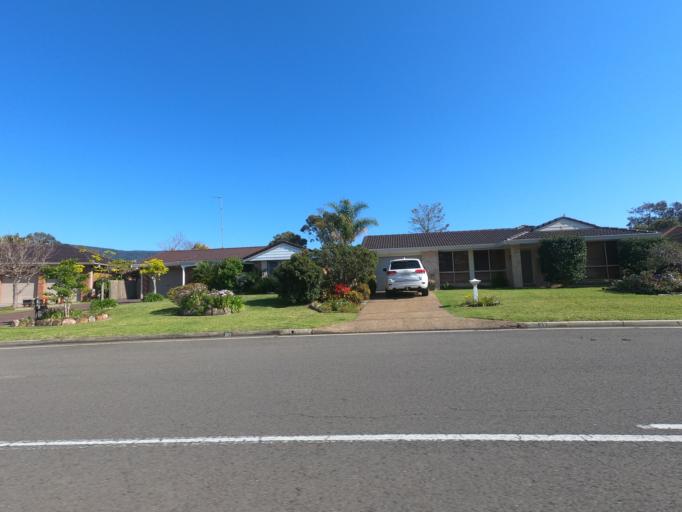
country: AU
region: New South Wales
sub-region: Wollongong
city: Dapto
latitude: -34.4892
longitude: 150.7778
